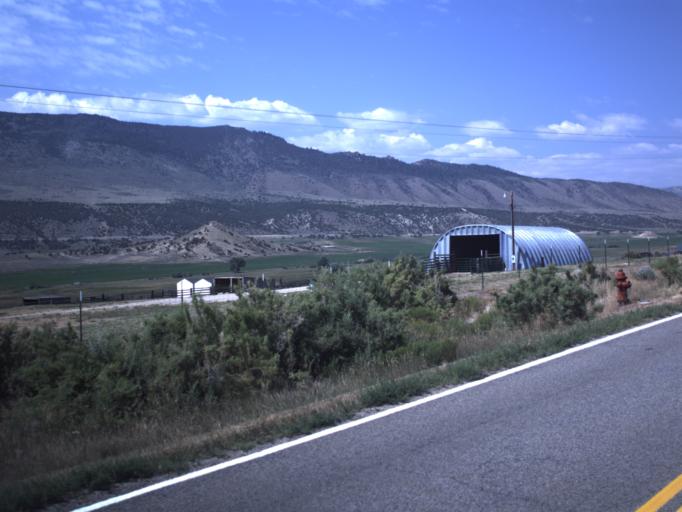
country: US
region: Utah
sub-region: Daggett County
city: Manila
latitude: 40.9766
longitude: -109.7744
